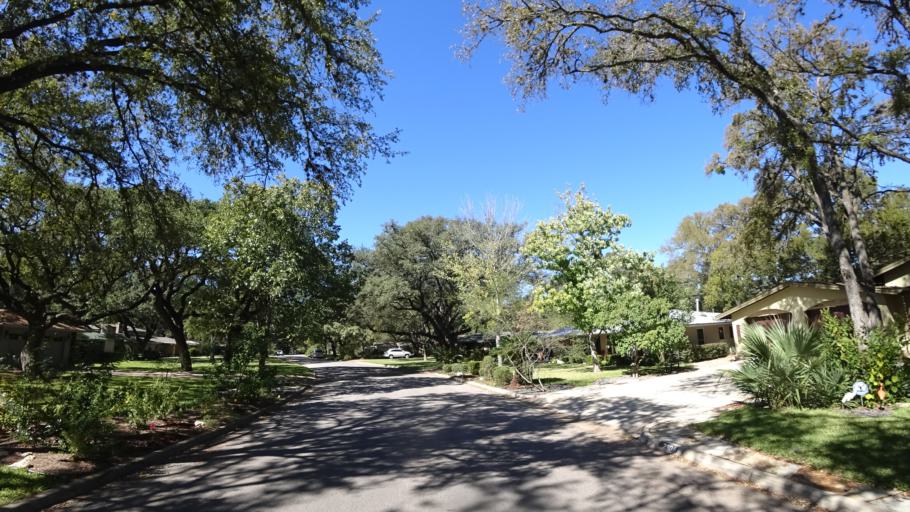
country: US
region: Texas
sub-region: Travis County
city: Austin
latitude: 30.3194
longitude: -97.7464
